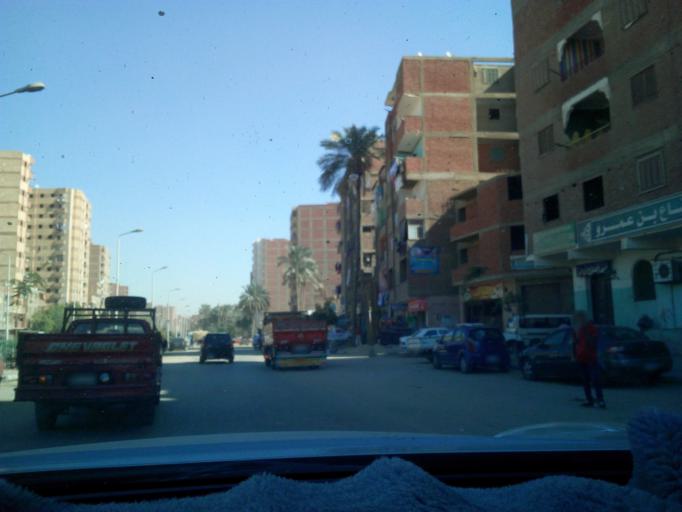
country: EG
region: Muhafazat al Qalyubiyah
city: Al Khankah
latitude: 30.1411
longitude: 31.3459
